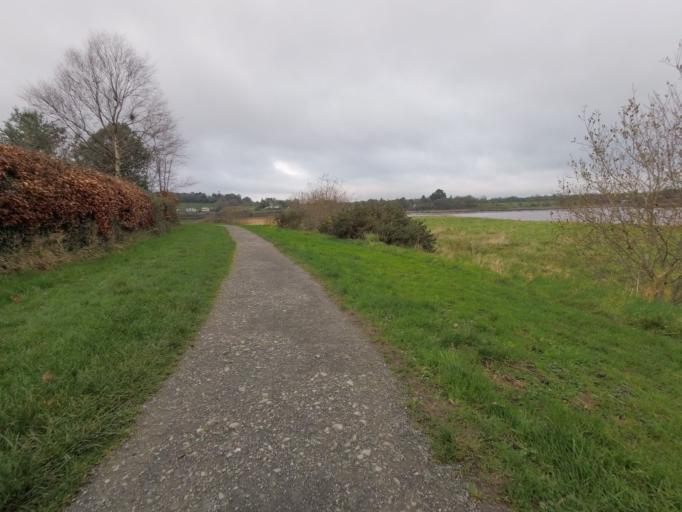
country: IE
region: Munster
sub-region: Waterford
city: Waterford
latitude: 52.2538
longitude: -7.0679
